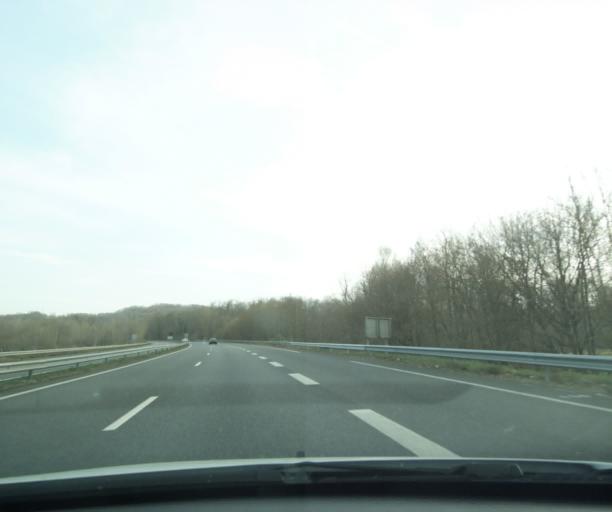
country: FR
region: Midi-Pyrenees
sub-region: Departement des Hautes-Pyrenees
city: Tournay
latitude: 43.1803
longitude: 0.2243
